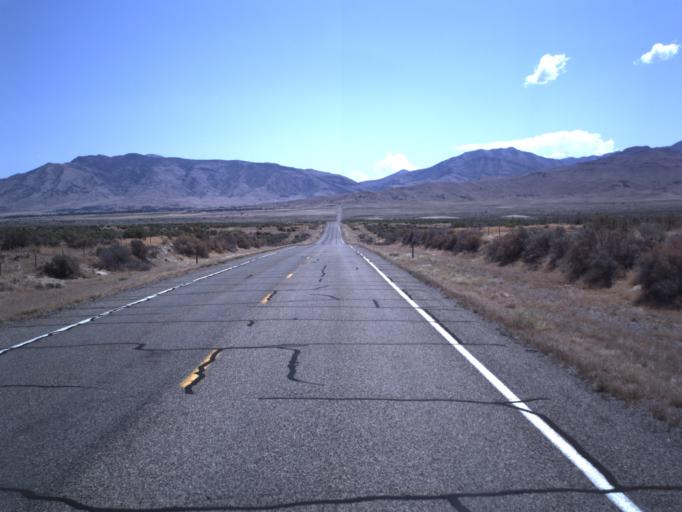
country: US
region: Utah
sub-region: Millard County
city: Delta
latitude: 39.3541
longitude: -112.4295
